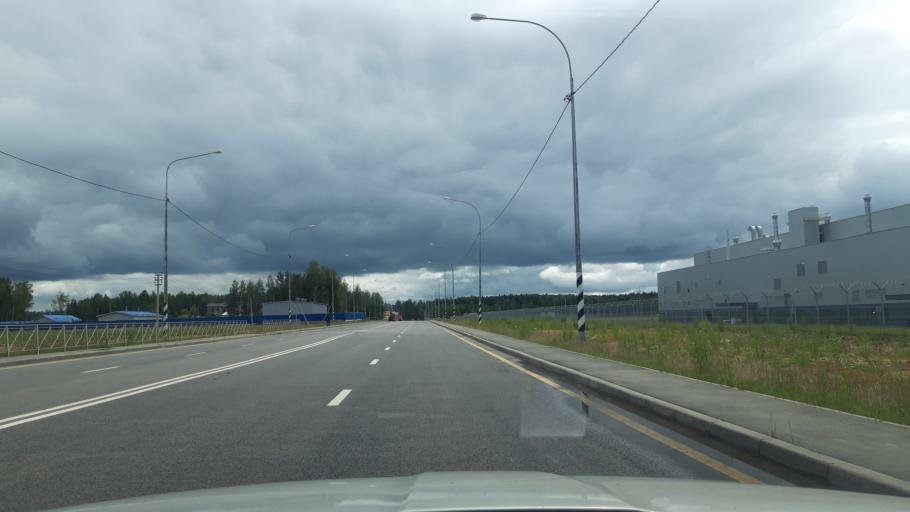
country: RU
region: Moskovskaya
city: Lozhki
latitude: 56.0853
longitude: 37.0836
